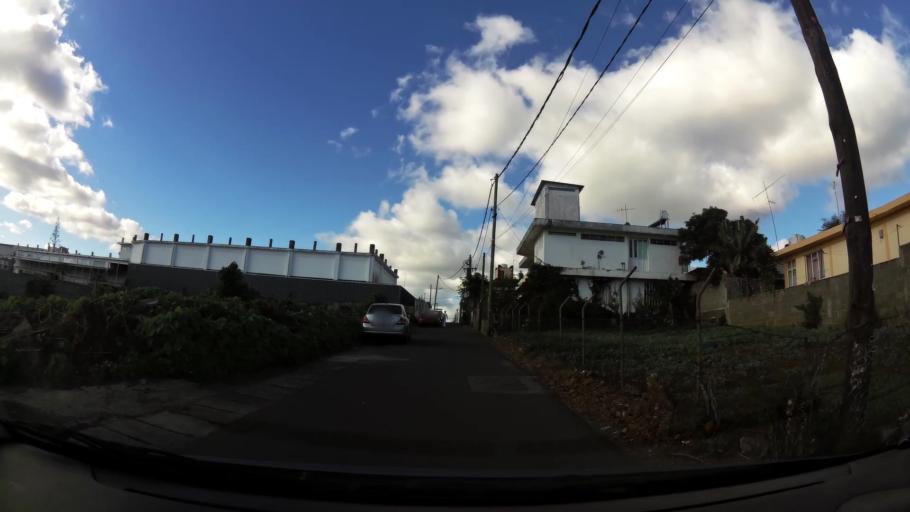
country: MU
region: Plaines Wilhems
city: Vacoas
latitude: -20.2934
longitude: 57.4843
